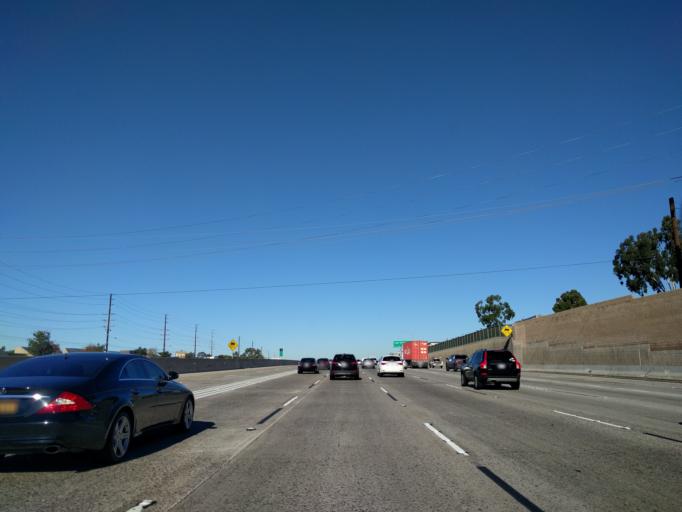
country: US
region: California
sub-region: Orange County
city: Laguna Hills
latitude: 33.6220
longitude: -117.7144
